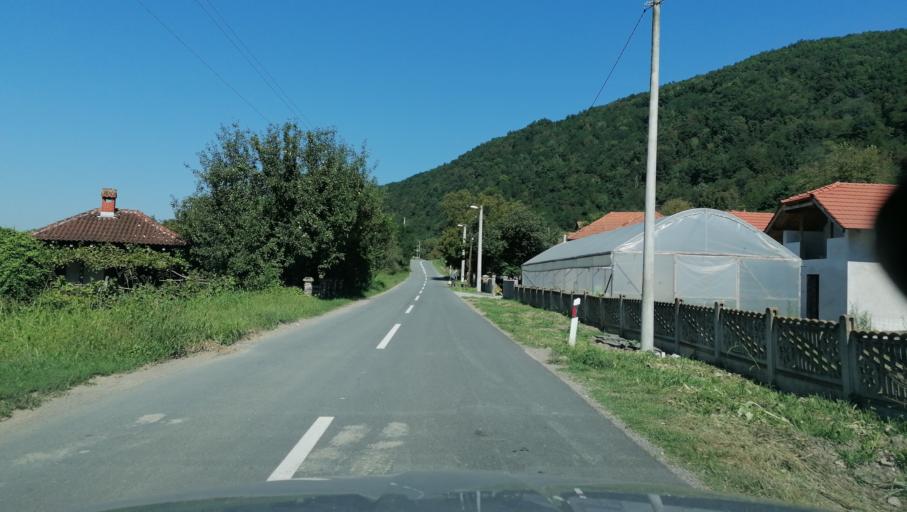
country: RS
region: Central Serbia
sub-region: Raski Okrug
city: Vrnjacka Banja
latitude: 43.6570
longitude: 20.9331
